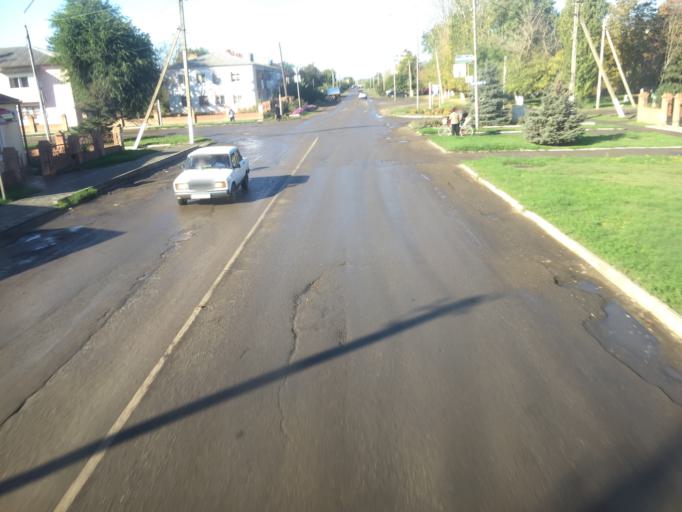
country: RU
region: Rostov
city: Peschanokopskoye
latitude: 46.1913
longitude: 41.0878
